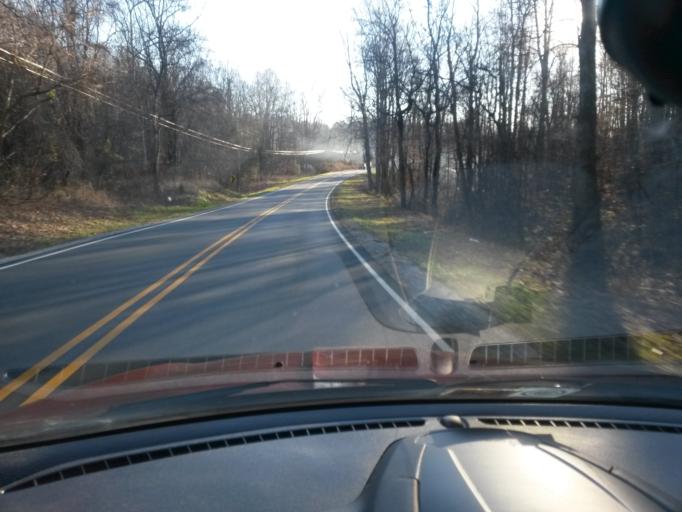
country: US
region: Virginia
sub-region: Amherst County
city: Amherst
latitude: 37.6194
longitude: -79.0963
